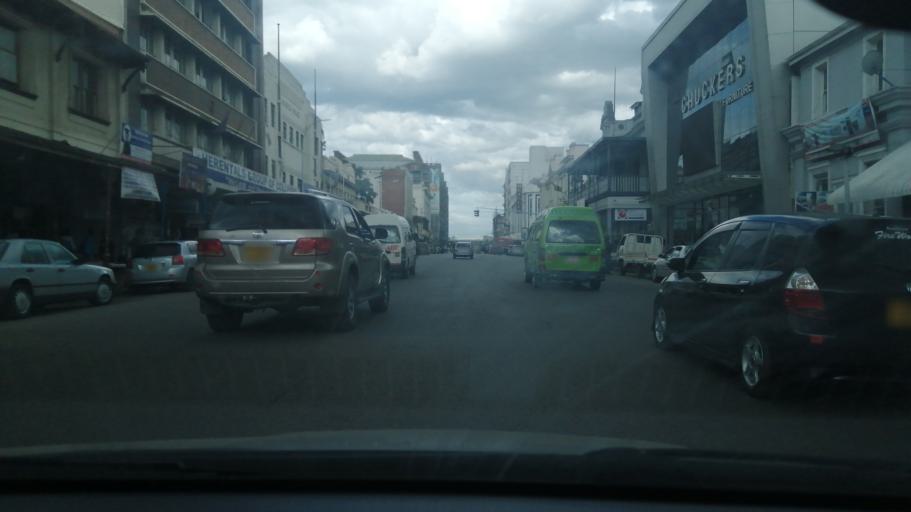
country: ZW
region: Harare
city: Harare
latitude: -17.8326
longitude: 31.0494
